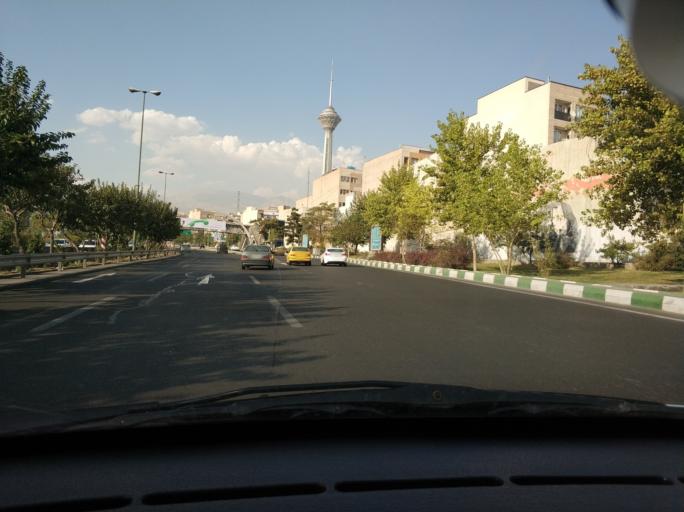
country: IR
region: Tehran
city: Tehran
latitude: 35.7326
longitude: 51.3714
